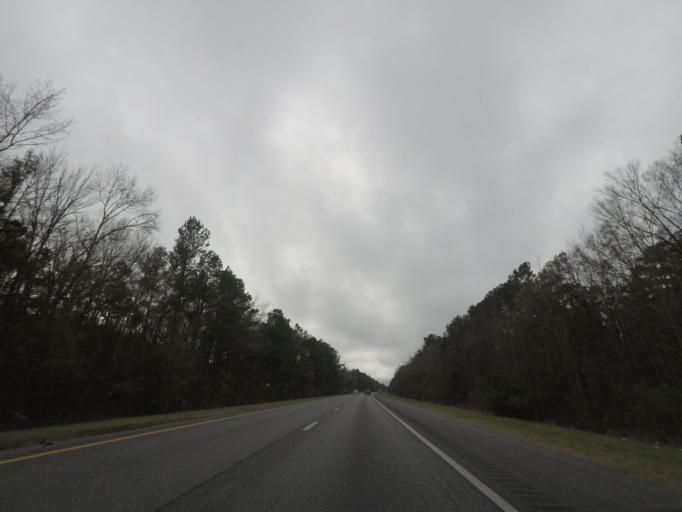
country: US
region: South Carolina
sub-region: Orangeburg County
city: Holly Hill
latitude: 33.3569
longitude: -80.5284
